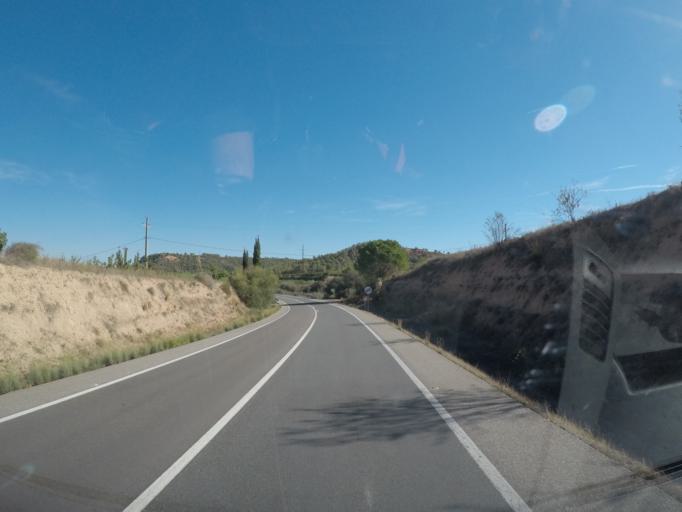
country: ES
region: Catalonia
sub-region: Provincia de Tarragona
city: Ginestar
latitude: 41.0490
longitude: 0.6579
